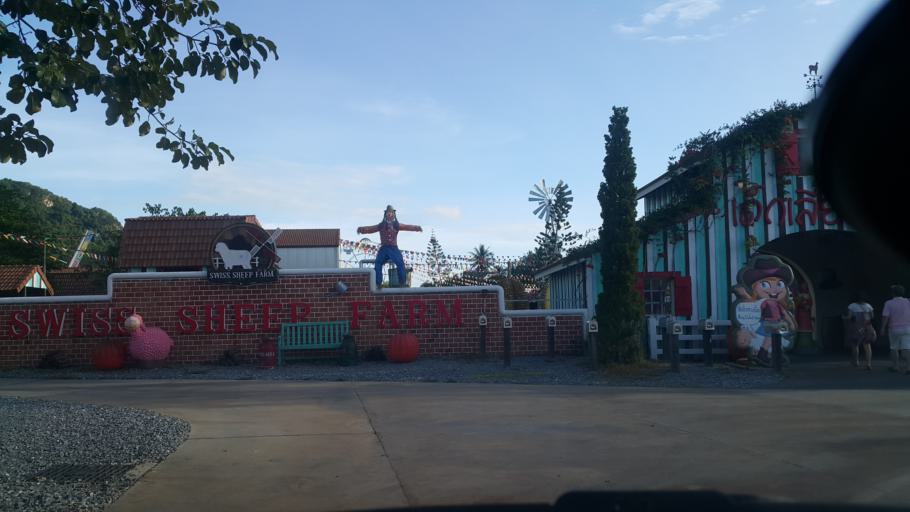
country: TH
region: Chon Buri
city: Sattahip
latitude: 12.7737
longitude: 100.9453
